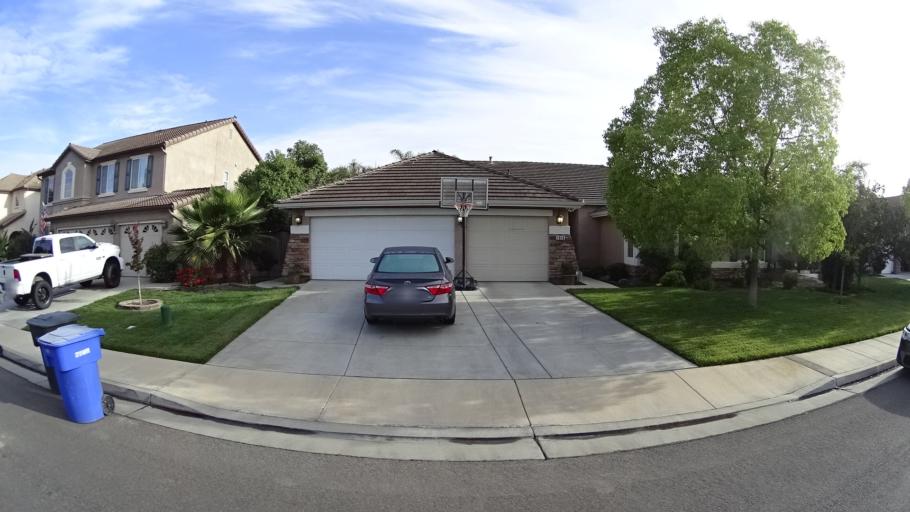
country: US
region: California
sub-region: Kings County
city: Hanford
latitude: 36.3469
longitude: -119.6750
